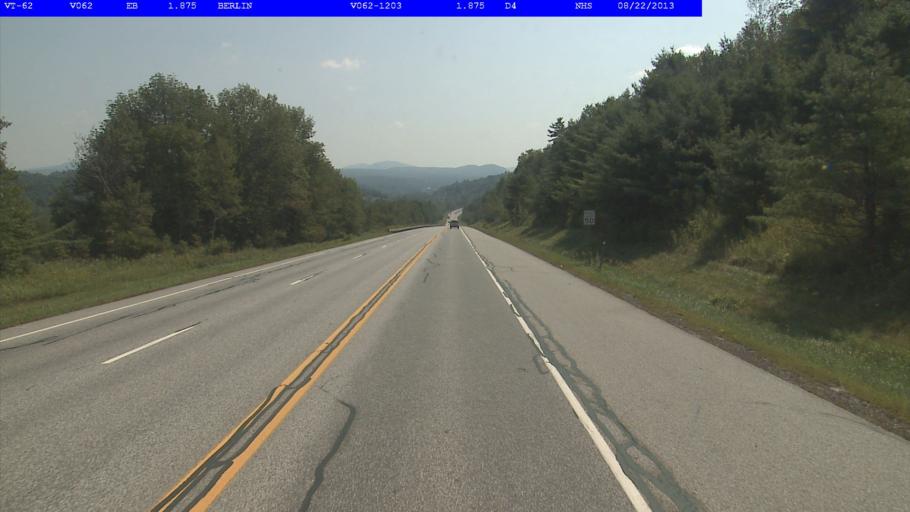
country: US
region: Vermont
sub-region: Washington County
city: Montpelier
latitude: 44.2203
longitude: -72.5524
